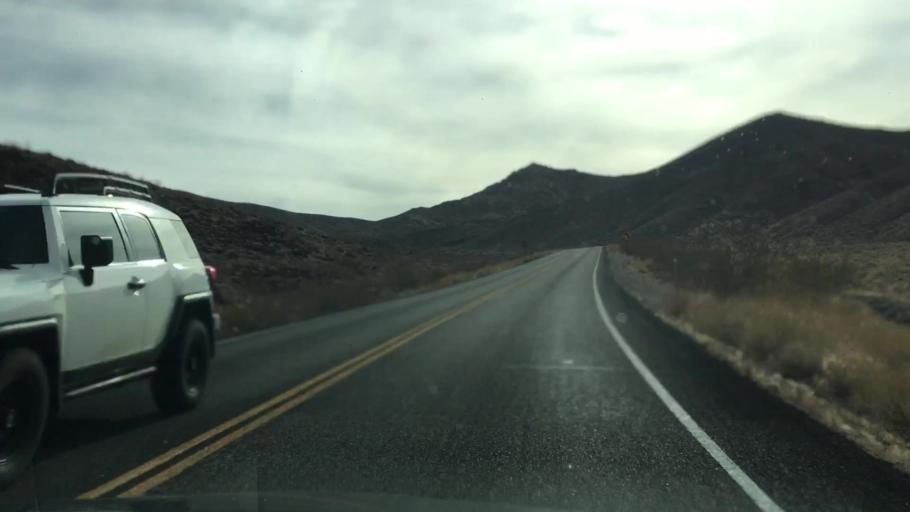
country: US
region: Nevada
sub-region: Nye County
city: Beatty
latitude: 36.7476
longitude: -116.9501
